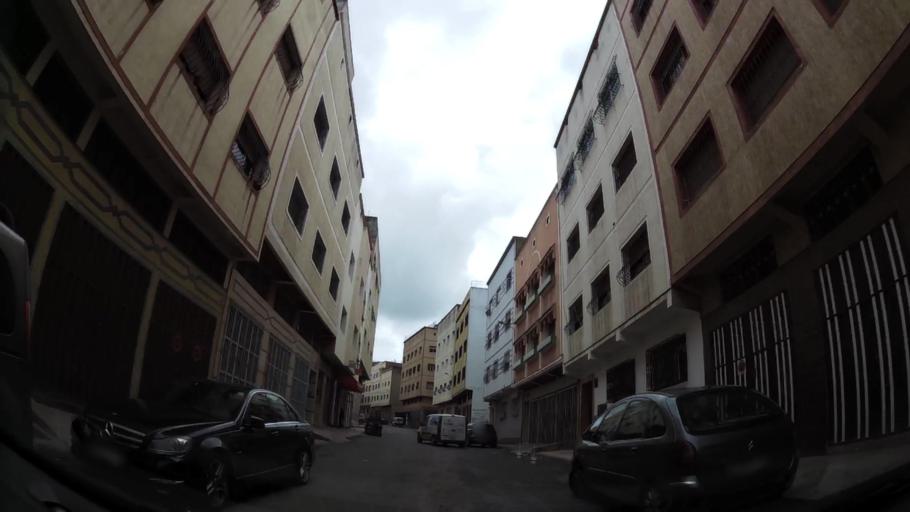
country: MA
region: Grand Casablanca
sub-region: Casablanca
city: Casablanca
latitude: 33.5329
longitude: -7.5916
